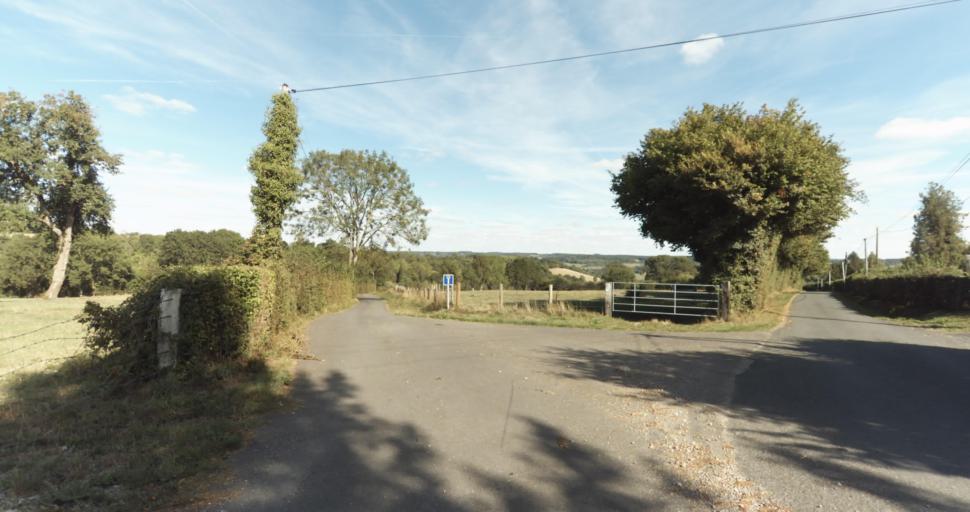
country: FR
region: Lower Normandy
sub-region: Departement de l'Orne
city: Vimoutiers
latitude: 48.9069
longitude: 0.1571
